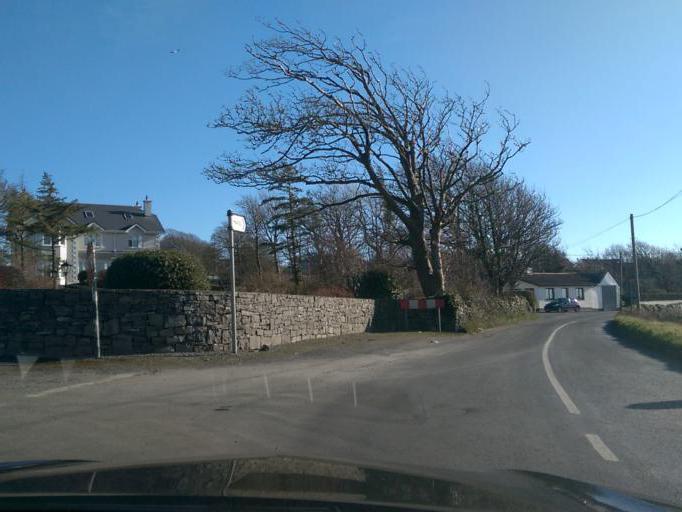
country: IE
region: Connaught
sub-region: County Galway
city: Oranmore
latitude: 53.2391
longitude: -8.9441
